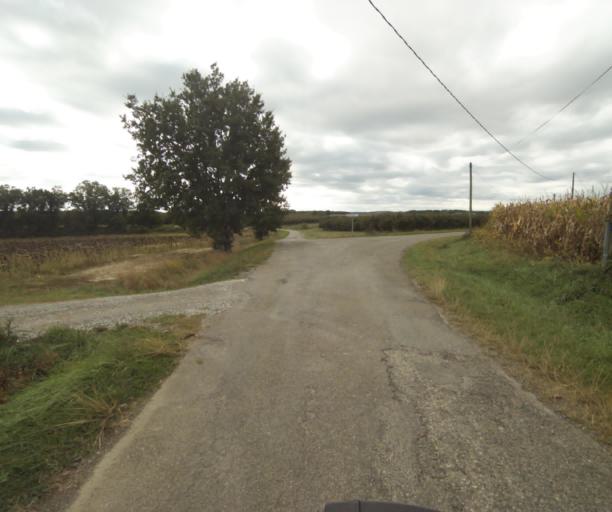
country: FR
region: Midi-Pyrenees
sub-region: Departement du Tarn-et-Garonne
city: Verdun-sur-Garonne
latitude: 43.8679
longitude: 1.1606
